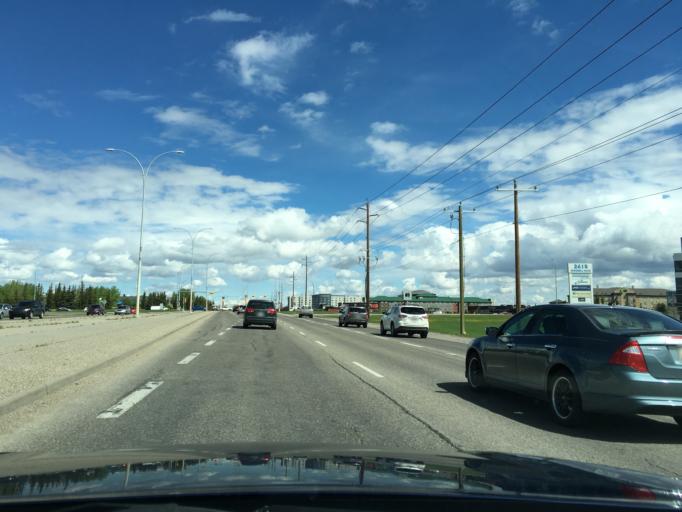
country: CA
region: Alberta
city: Calgary
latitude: 51.0908
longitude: -114.0015
